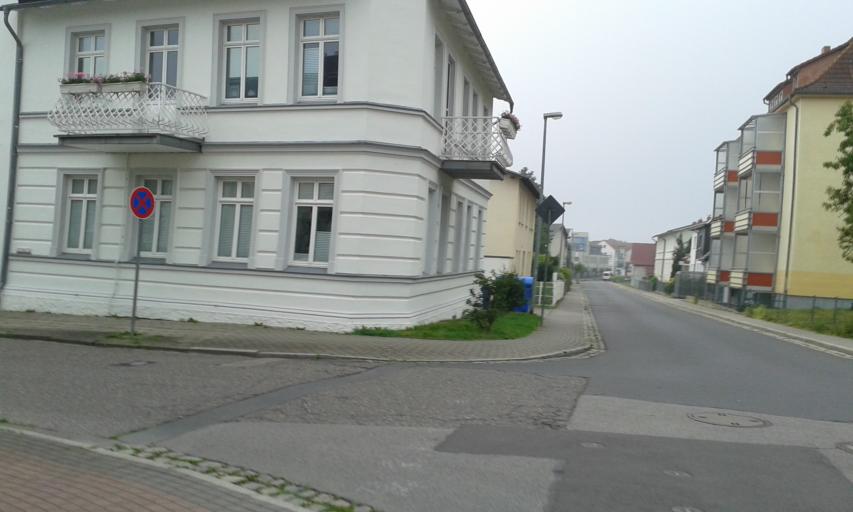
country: DE
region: Mecklenburg-Vorpommern
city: Sassnitz
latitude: 54.5173
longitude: 13.6436
